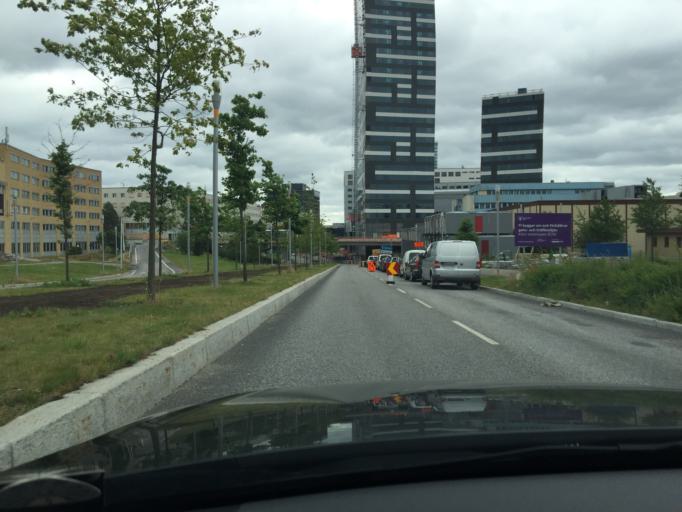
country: SE
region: Stockholm
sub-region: Stockholms Kommun
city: Kista
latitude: 59.4064
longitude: 17.9398
